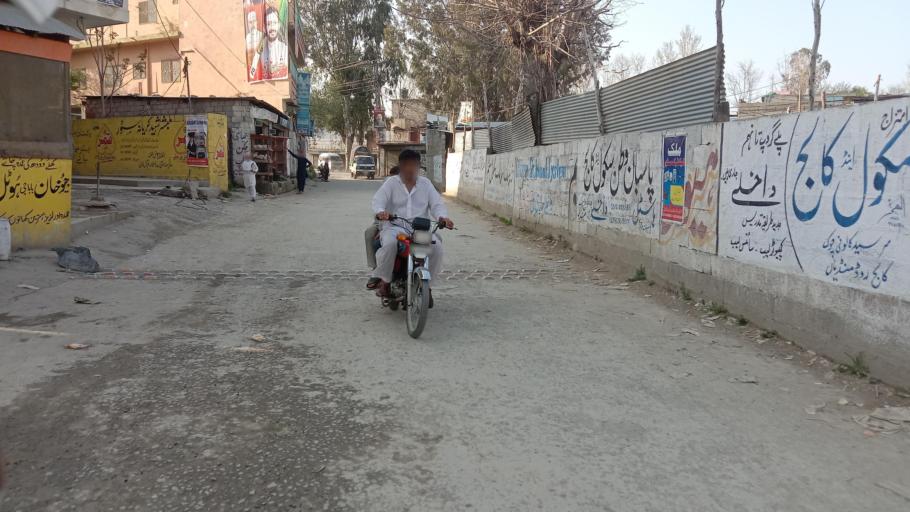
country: PK
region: Khyber Pakhtunkhwa
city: Abbottabad
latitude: 34.2015
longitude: 73.2260
